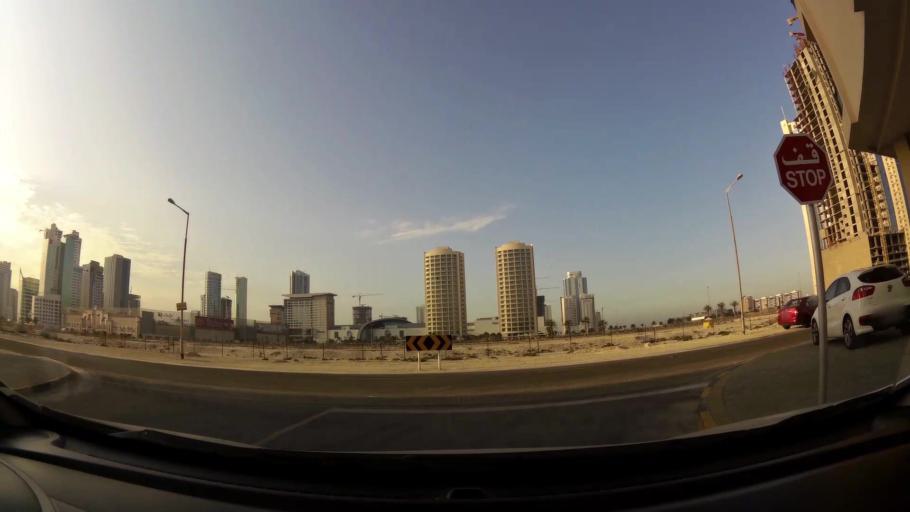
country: BH
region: Manama
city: Jidd Hafs
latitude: 26.2274
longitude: 50.5559
